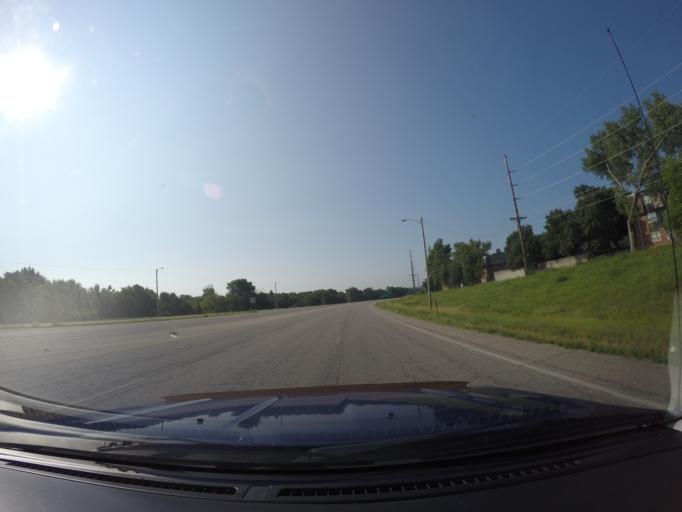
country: US
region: Kansas
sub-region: Riley County
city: Manhattan
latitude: 39.2012
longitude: -96.6139
